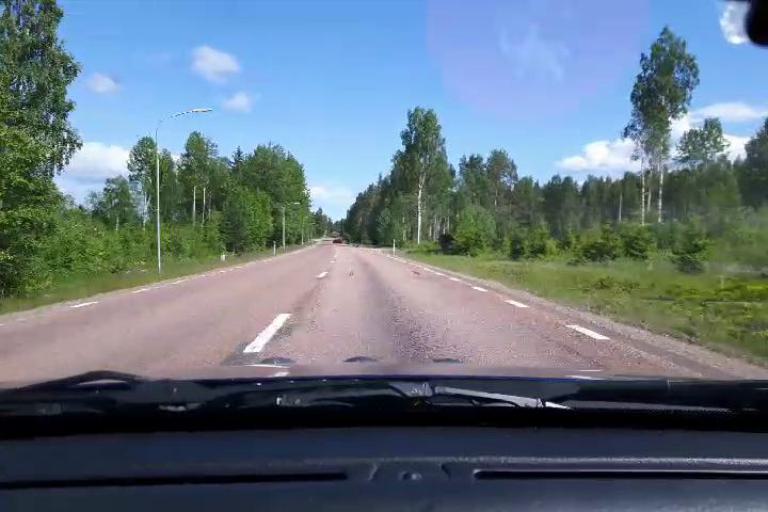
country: SE
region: Gaevleborg
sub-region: Hudiksvalls Kommun
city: Delsbo
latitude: 61.8017
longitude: 16.4805
